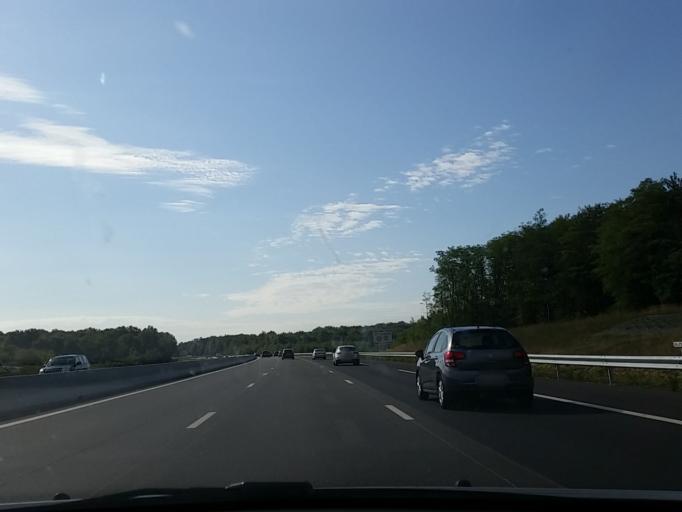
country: FR
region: Centre
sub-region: Departement du Cher
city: Vierzon
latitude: 47.2581
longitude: 2.0465
